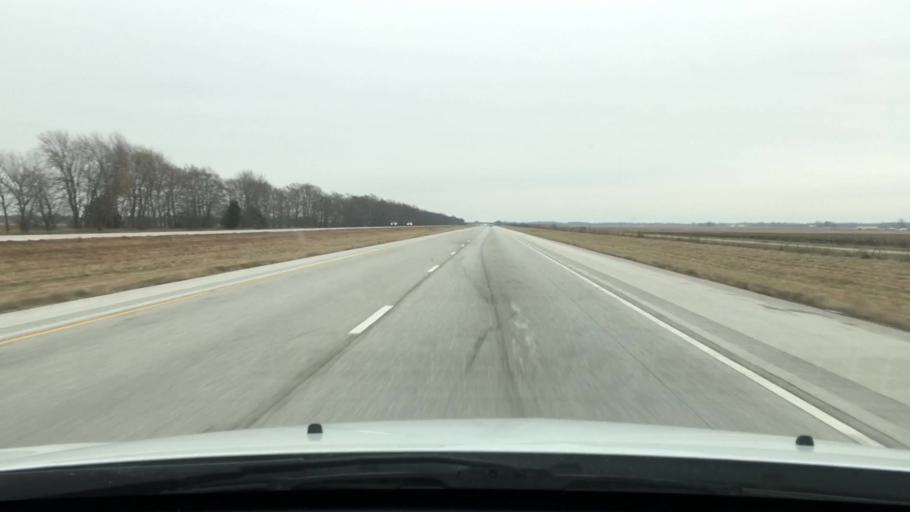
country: US
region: Illinois
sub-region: Scott County
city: Winchester
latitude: 39.6801
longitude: -90.3718
